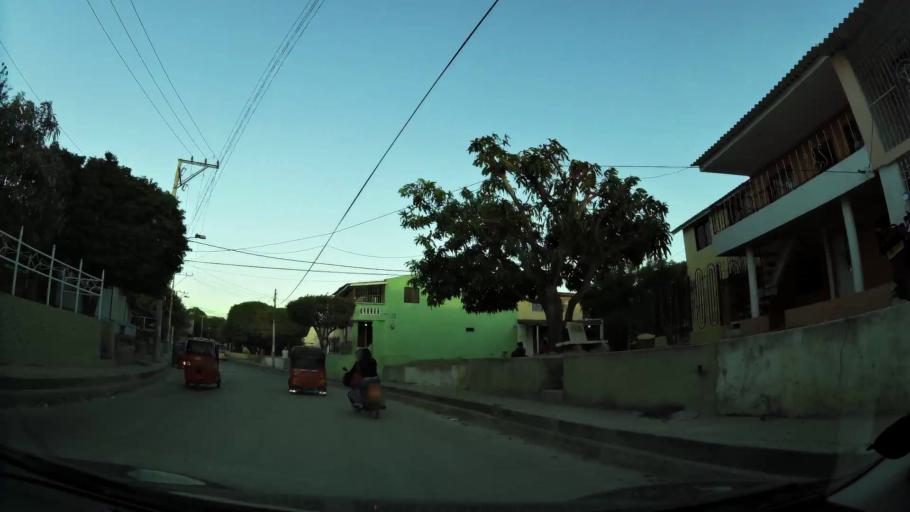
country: CO
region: Atlantico
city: Soledad
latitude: 10.9248
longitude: -74.7837
